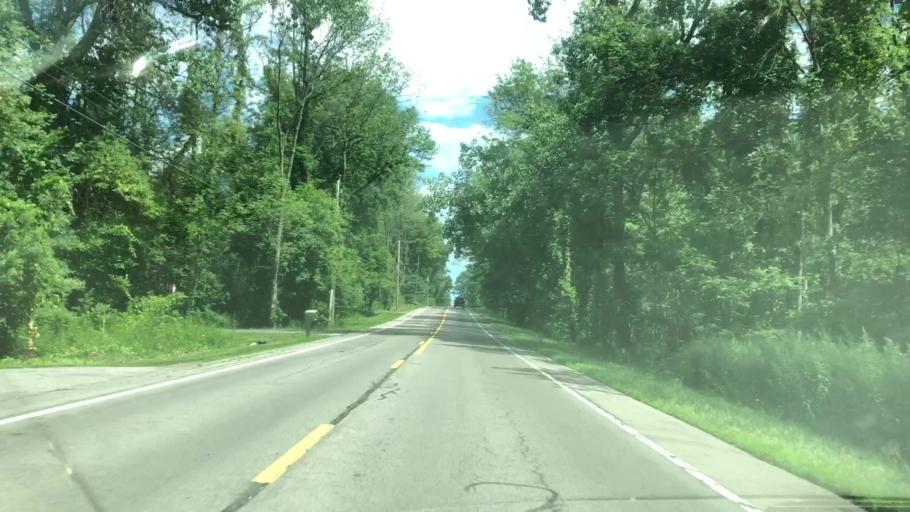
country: US
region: New York
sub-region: Monroe County
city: Webster
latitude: 43.1599
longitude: -77.4240
